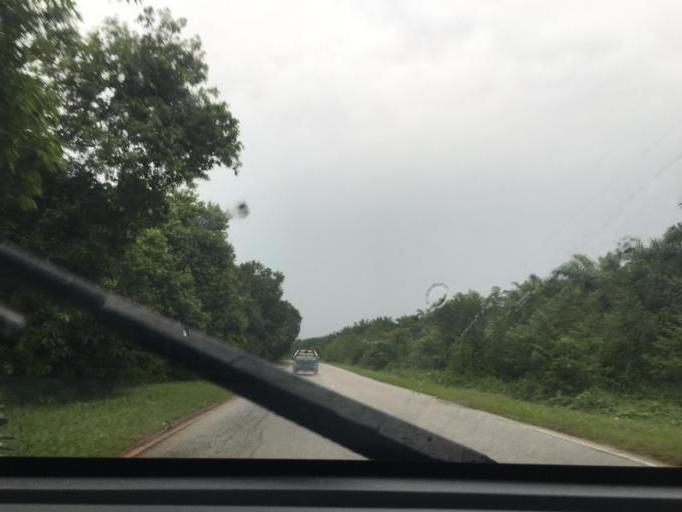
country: MY
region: Kedah
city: Sungai Petani
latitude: 5.6326
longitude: 100.6311
